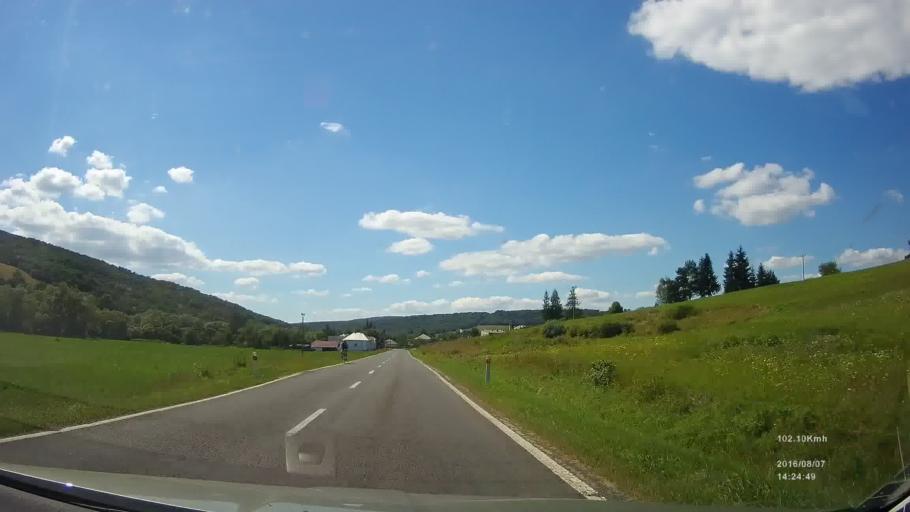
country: SK
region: Presovsky
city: Stropkov
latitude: 49.2652
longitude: 21.7248
